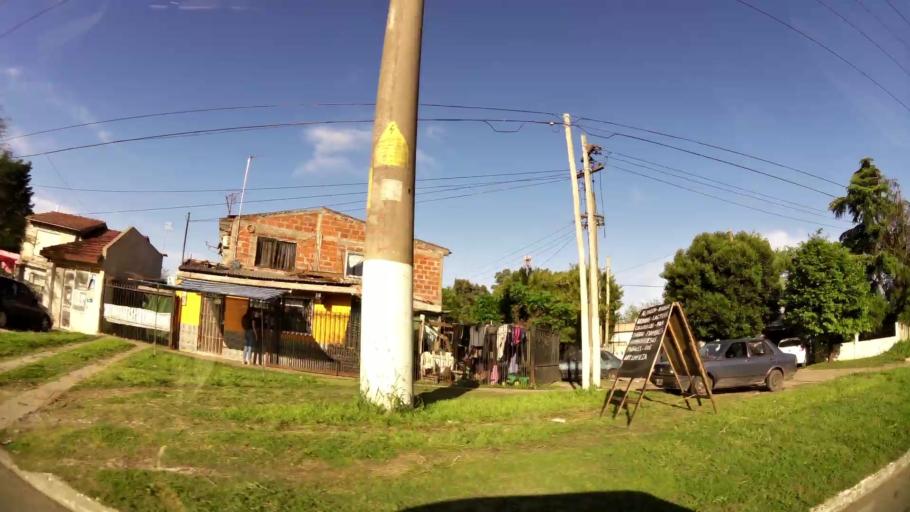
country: AR
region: Buenos Aires
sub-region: Partido de Quilmes
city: Quilmes
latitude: -34.8044
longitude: -58.2069
